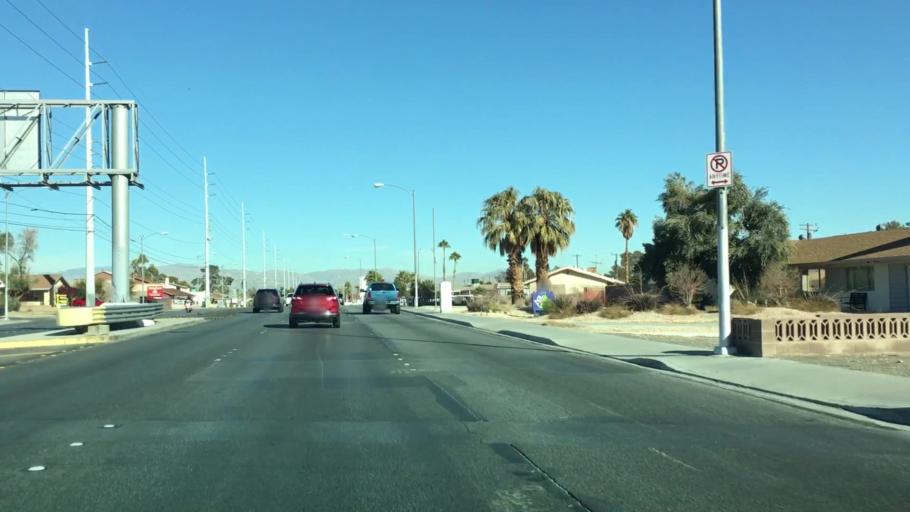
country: US
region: Nevada
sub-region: Clark County
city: Paradise
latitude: 36.0886
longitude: -115.1187
